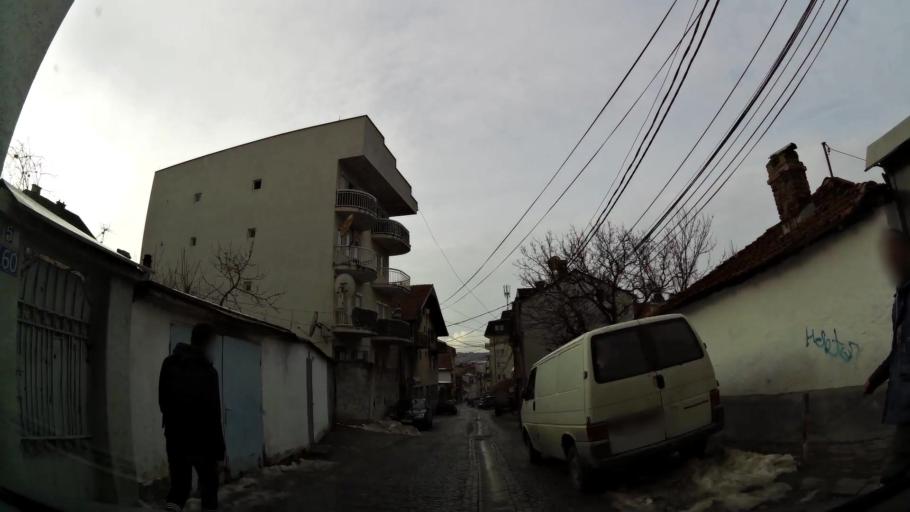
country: XK
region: Pristina
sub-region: Komuna e Prishtines
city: Pristina
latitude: 42.6691
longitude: 21.1696
